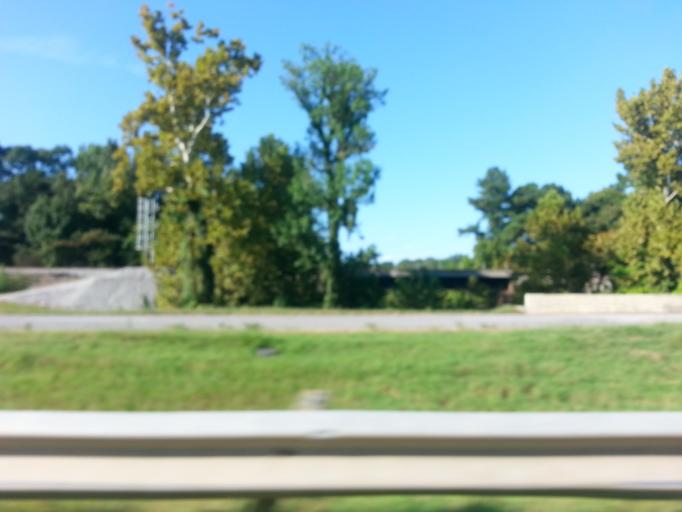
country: US
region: Alabama
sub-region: Colbert County
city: Tuscumbia
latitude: 34.7196
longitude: -87.8007
